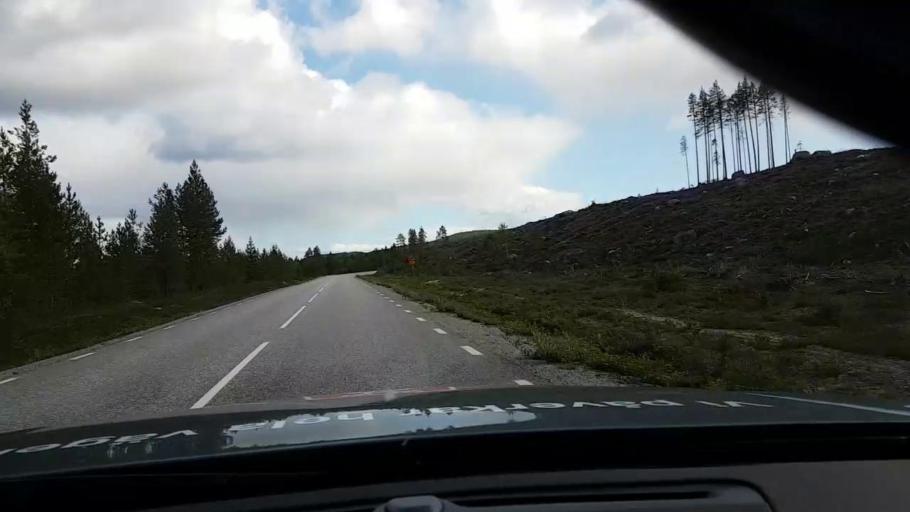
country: SE
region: Vaesternorrland
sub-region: OErnskoeldsviks Kommun
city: Bredbyn
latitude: 63.6794
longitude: 17.7878
